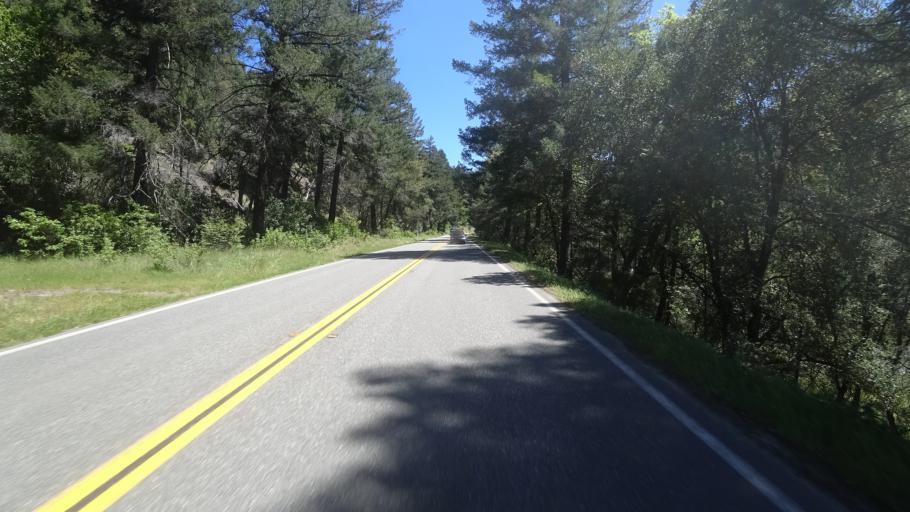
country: US
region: California
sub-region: Trinity County
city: Hayfork
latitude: 40.7501
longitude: -123.2767
